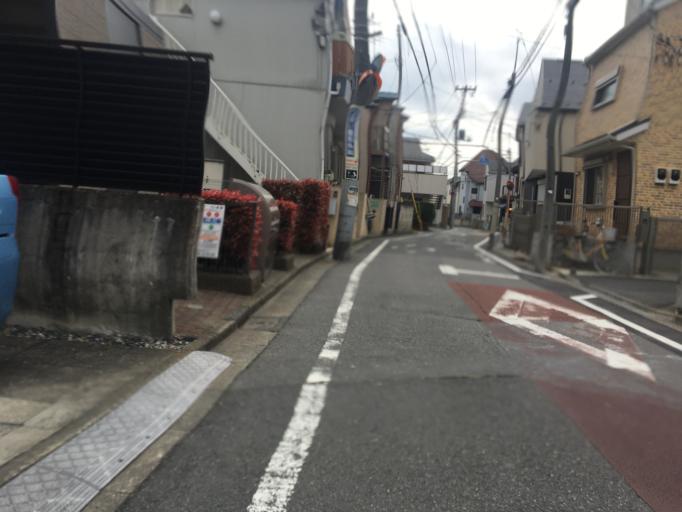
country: JP
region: Tokyo
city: Tokyo
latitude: 35.7183
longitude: 139.6469
